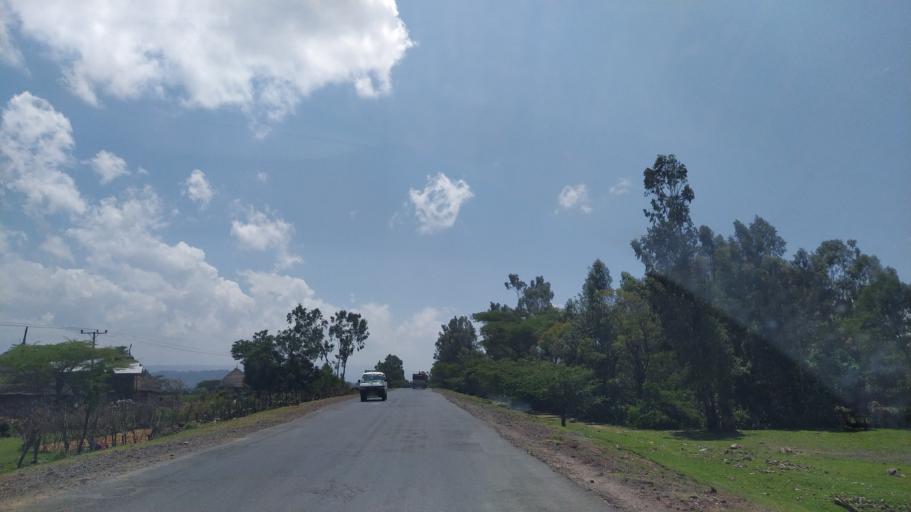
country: ET
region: Southern Nations, Nationalities, and People's Region
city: Butajira
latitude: 7.7627
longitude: 38.1342
